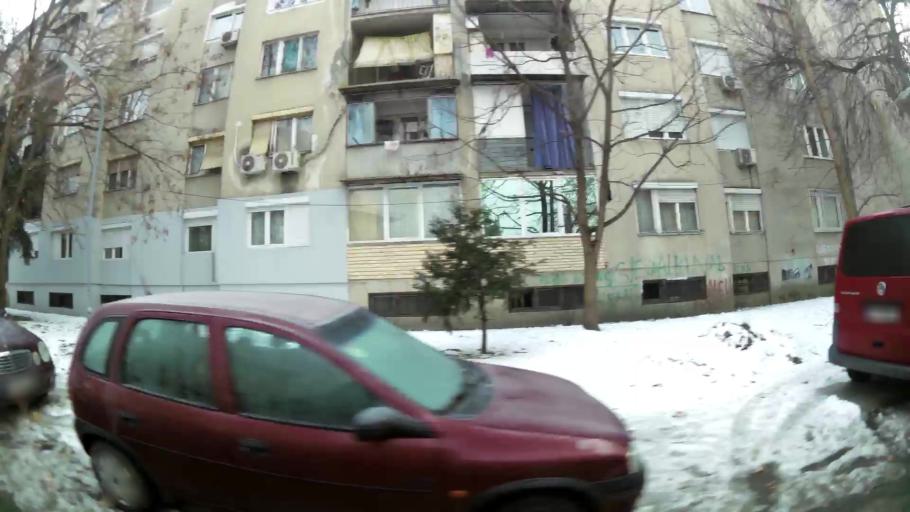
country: MK
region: Cair
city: Cair
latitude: 42.0186
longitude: 21.4455
